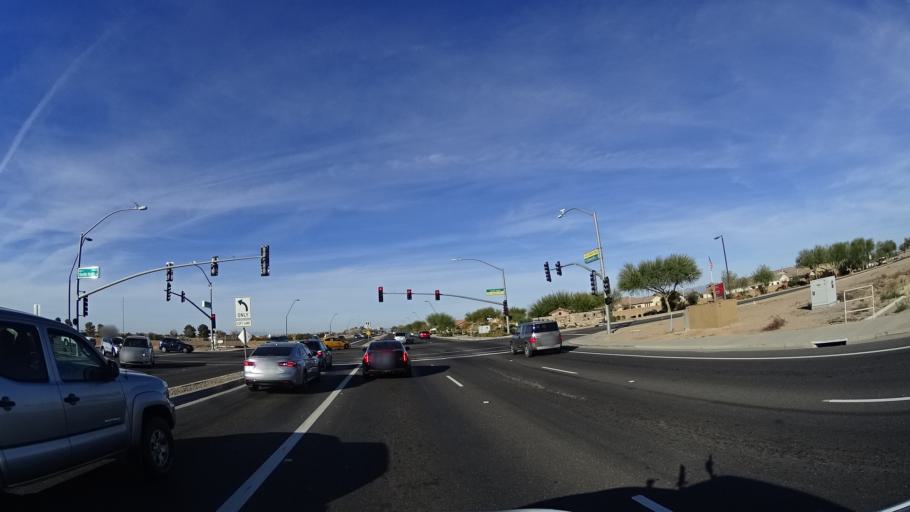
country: US
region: Arizona
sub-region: Maricopa County
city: Queen Creek
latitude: 33.2337
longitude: -111.6345
